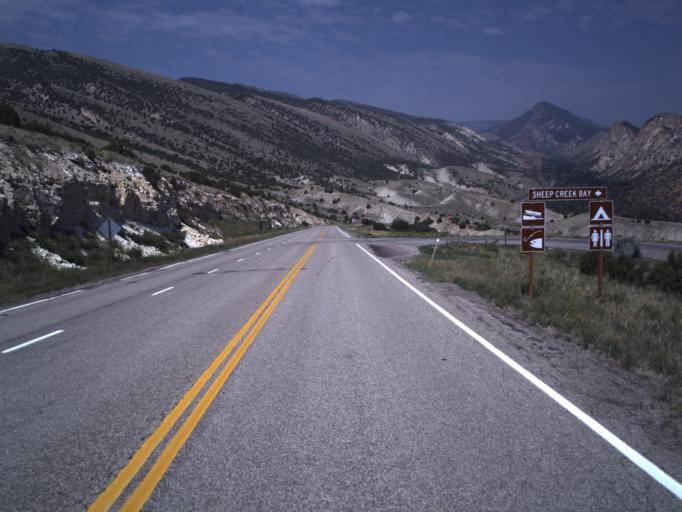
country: US
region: Utah
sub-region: Daggett County
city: Manila
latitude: 40.9157
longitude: -109.6832
